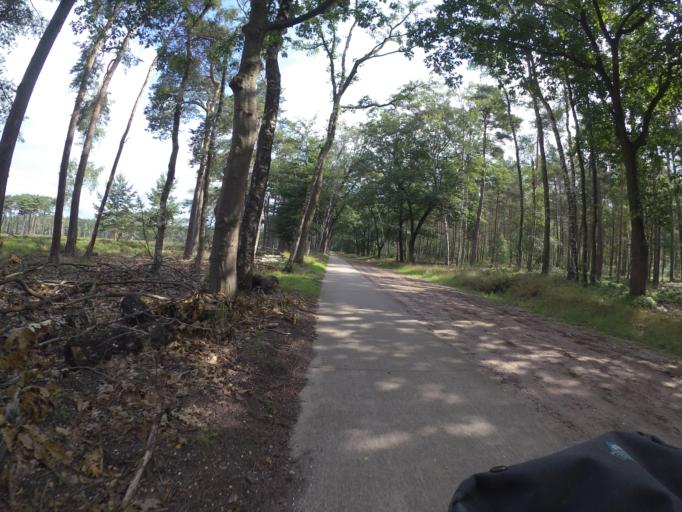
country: NL
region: Gelderland
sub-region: Gemeente Epe
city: Emst
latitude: 52.3402
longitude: 5.9100
